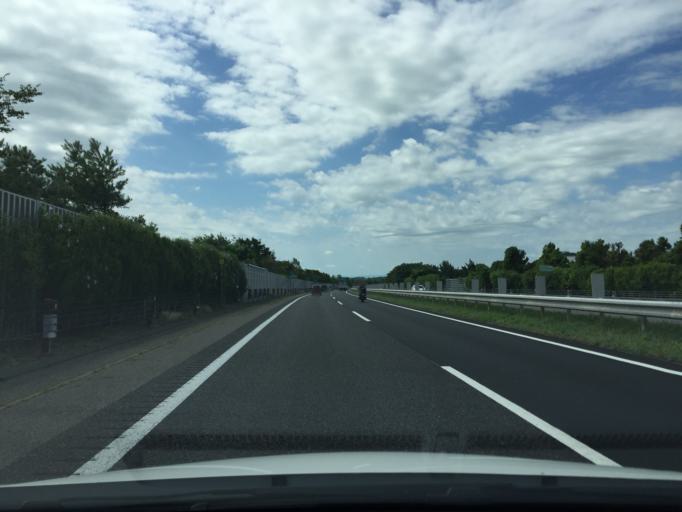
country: JP
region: Fukushima
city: Koriyama
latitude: 37.3843
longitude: 140.3127
